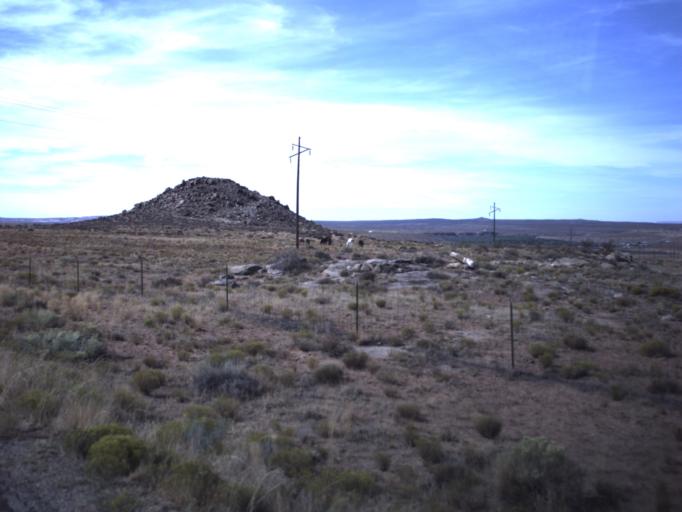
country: US
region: Utah
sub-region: San Juan County
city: Blanding
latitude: 37.2768
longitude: -109.2967
